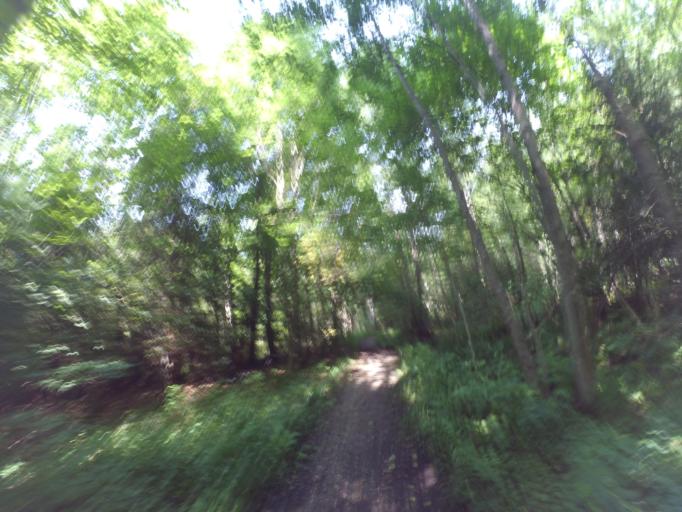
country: DE
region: Bavaria
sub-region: Swabia
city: Unteregg
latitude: 47.9629
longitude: 10.4506
